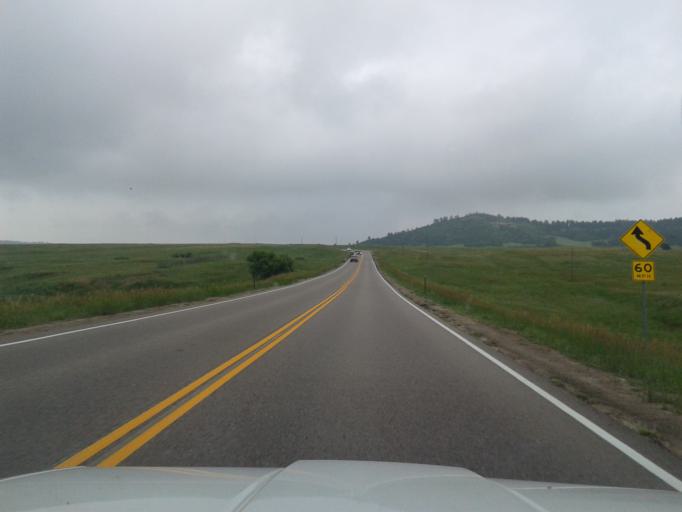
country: US
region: Colorado
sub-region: El Paso County
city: Woodmoor
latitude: 39.1530
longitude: -104.7543
